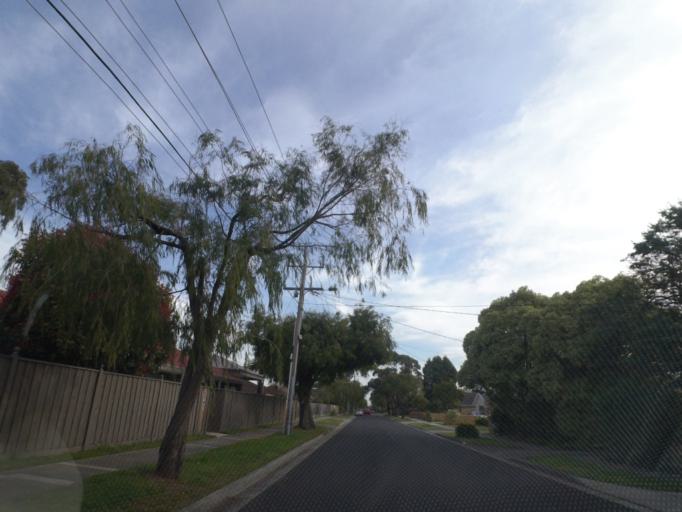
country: AU
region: Victoria
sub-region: Knox
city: Knoxfield
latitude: -37.8853
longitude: 145.2432
